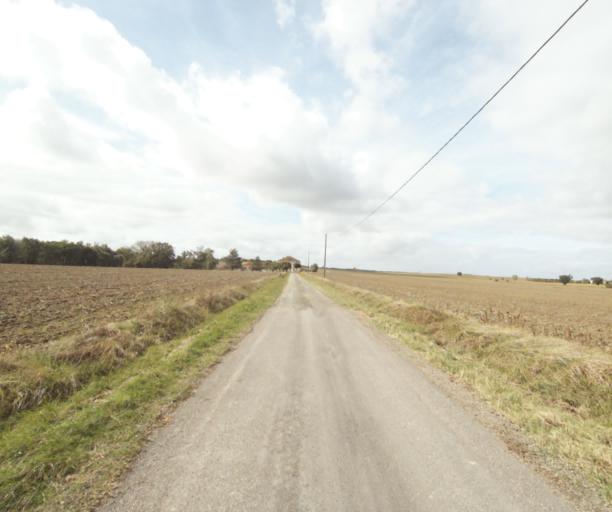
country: FR
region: Midi-Pyrenees
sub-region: Departement du Tarn-et-Garonne
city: Finhan
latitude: 43.8817
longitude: 1.1103
